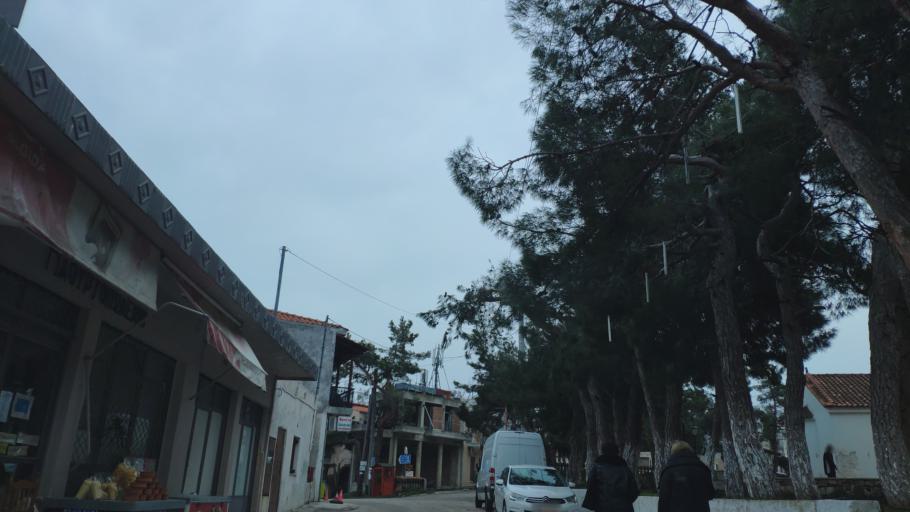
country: GR
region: Attica
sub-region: Nomarchia Dytikis Attikis
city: Vilia
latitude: 38.1672
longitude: 23.3377
